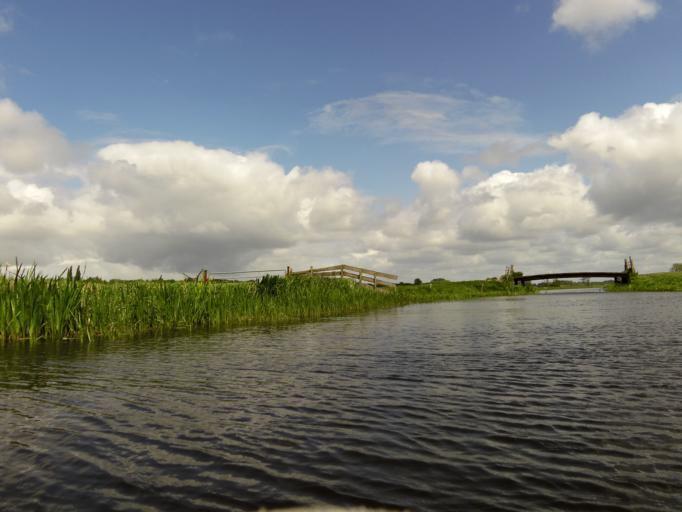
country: NL
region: South Holland
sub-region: Gemeente Leidschendam-Voorburg
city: Voorburg
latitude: 52.1046
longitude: 4.3754
